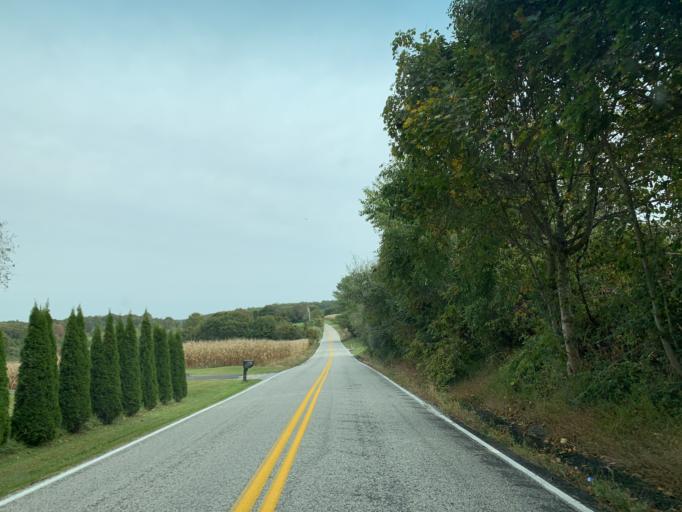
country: US
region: Pennsylvania
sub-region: York County
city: Susquehanna Trails
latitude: 39.7438
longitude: -76.4436
